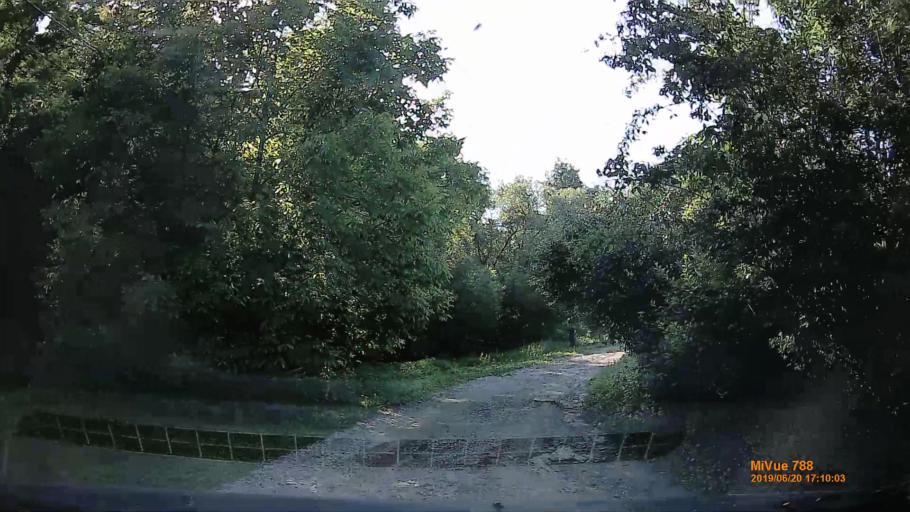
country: HU
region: Baranya
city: Buekkoesd
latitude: 46.1435
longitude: 18.0055
